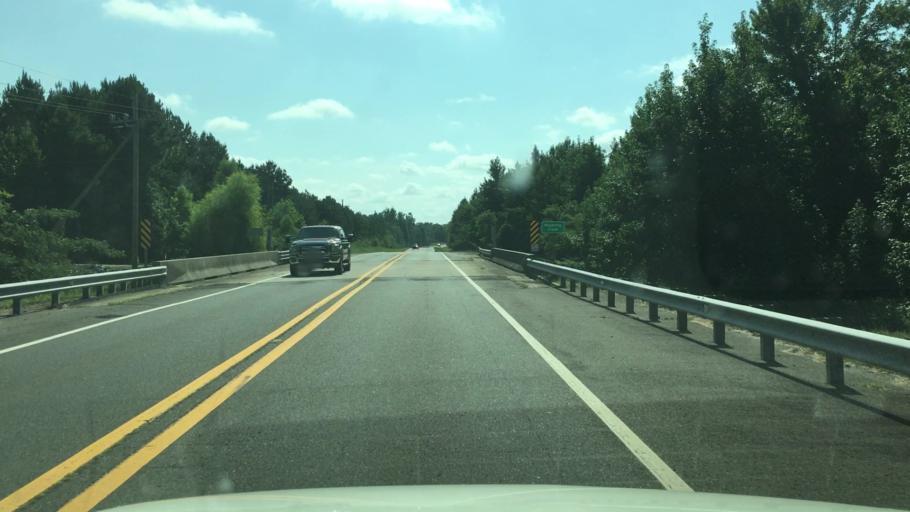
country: US
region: Arkansas
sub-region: Garland County
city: Rockwell
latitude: 34.5165
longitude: -93.2962
